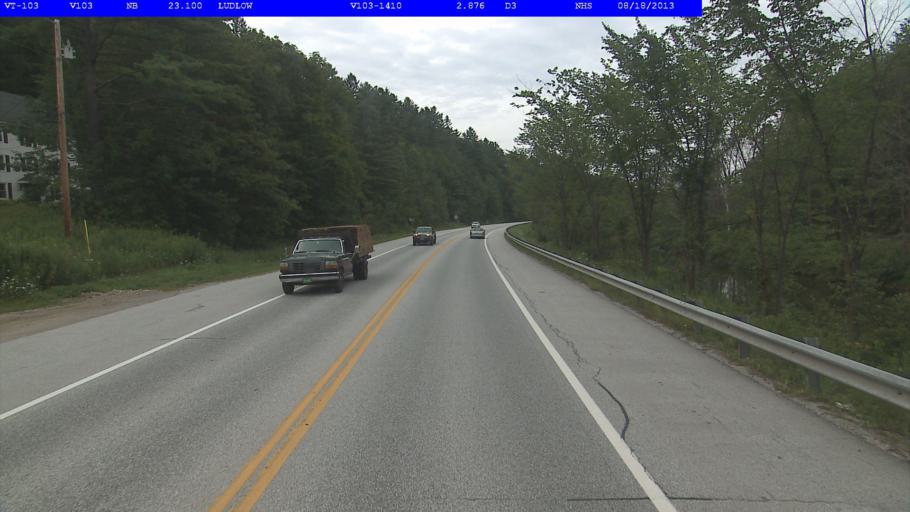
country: US
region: Vermont
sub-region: Windsor County
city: Chester
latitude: 43.4037
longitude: -72.7076
